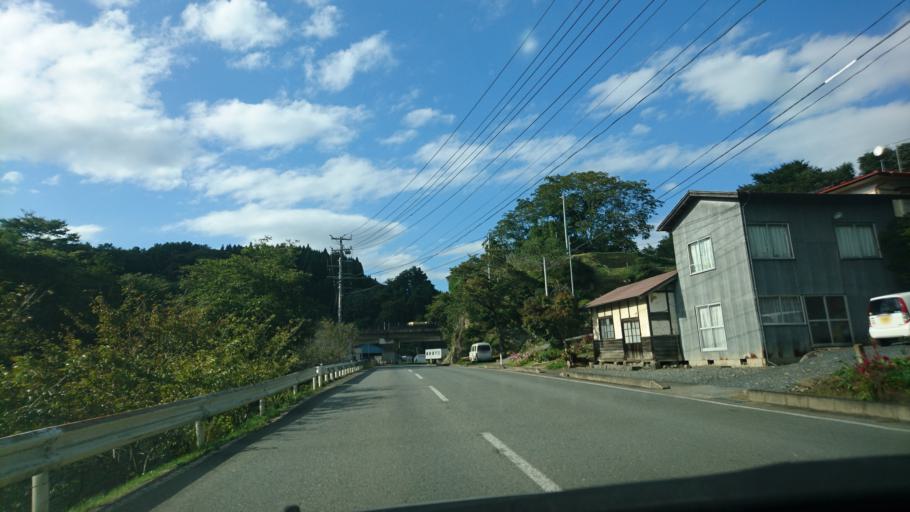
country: JP
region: Iwate
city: Ichinoseki
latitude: 38.9017
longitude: 141.3247
